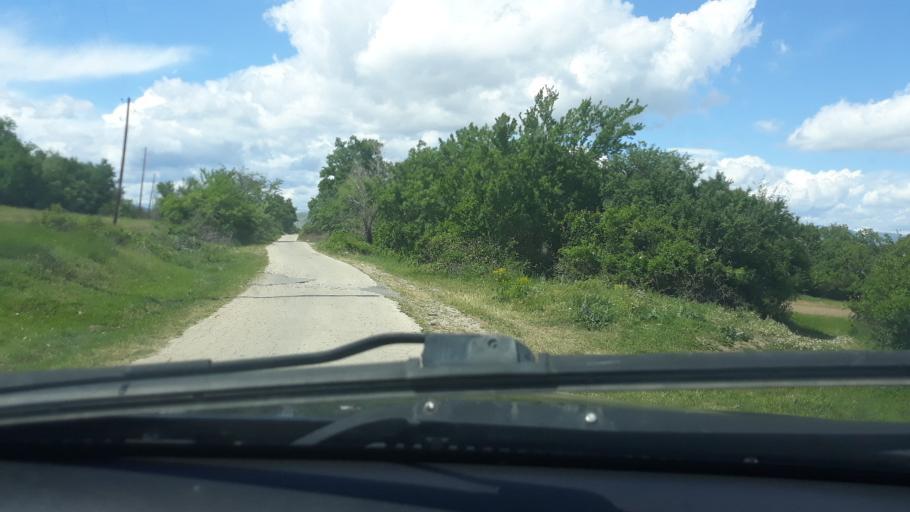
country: MK
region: Krivogastani
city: Krivogashtani
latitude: 41.3262
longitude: 21.3036
